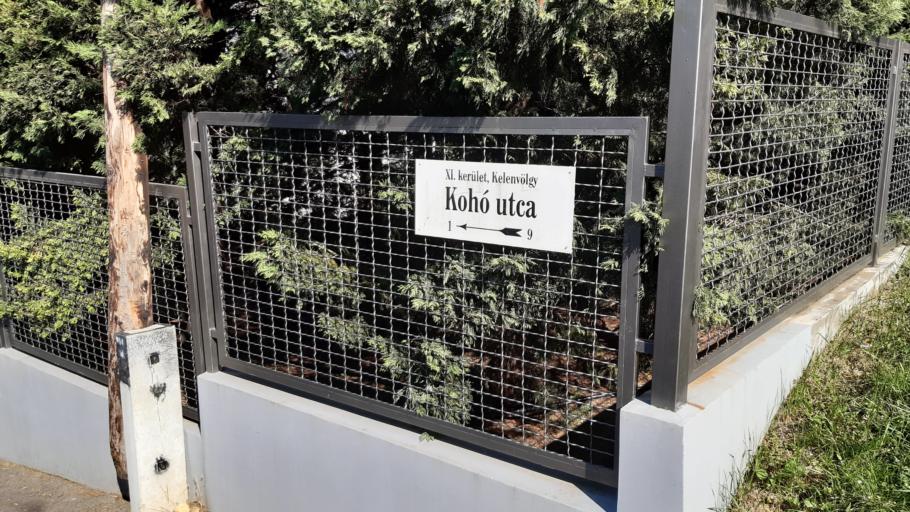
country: HU
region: Budapest
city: Budapest XXII. keruelet
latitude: 47.4477
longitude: 19.0212
